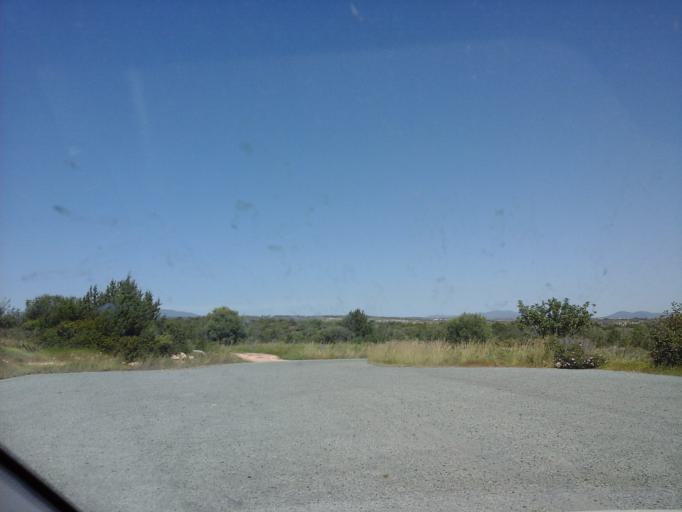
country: CY
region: Limassol
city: Sotira
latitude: 34.6728
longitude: 32.8648
